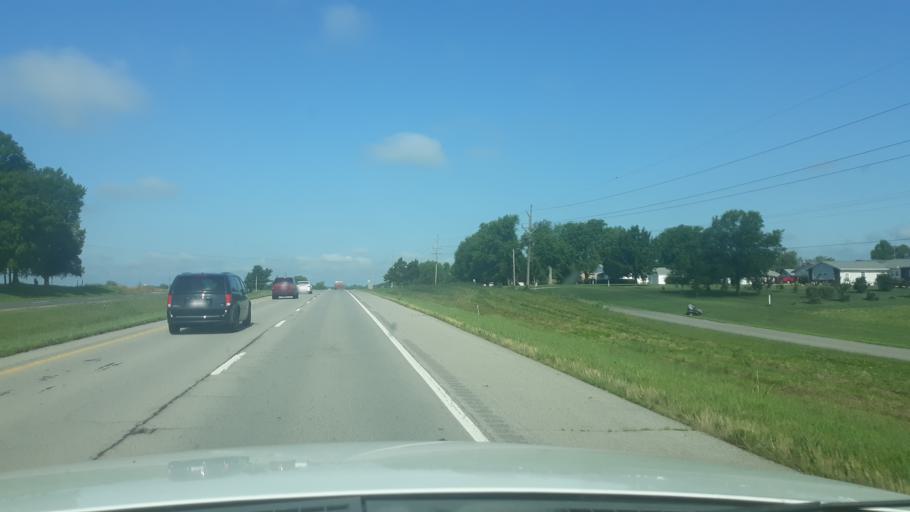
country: US
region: Illinois
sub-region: Williamson County
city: Marion
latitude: 37.7294
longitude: -88.8624
